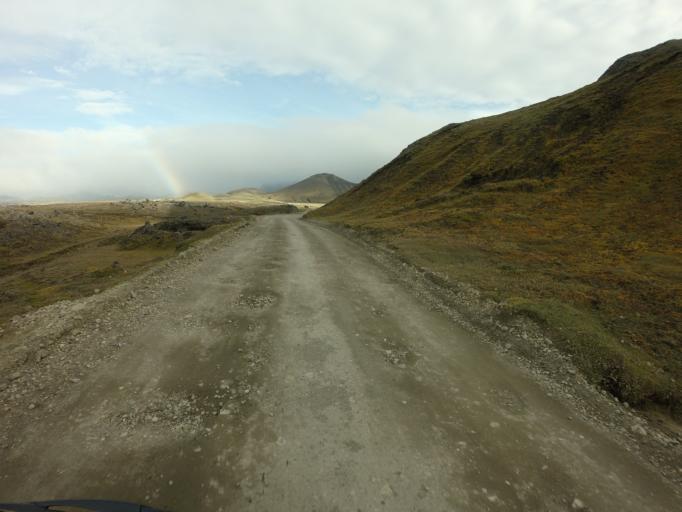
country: IS
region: South
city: Vestmannaeyjar
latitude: 64.0060
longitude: -19.0384
